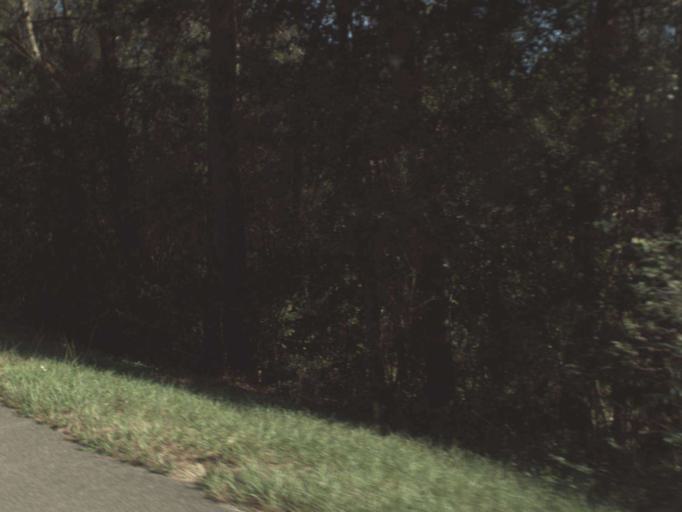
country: US
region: Florida
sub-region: Walton County
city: DeFuniak Springs
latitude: 30.6840
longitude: -85.9364
